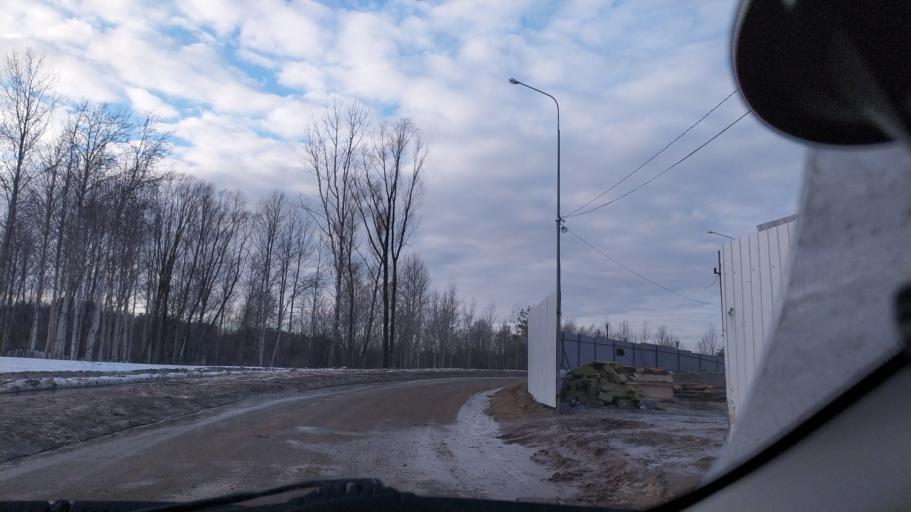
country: RU
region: Chuvashia
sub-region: Cheboksarskiy Rayon
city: Cheboksary
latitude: 56.1492
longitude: 47.2098
